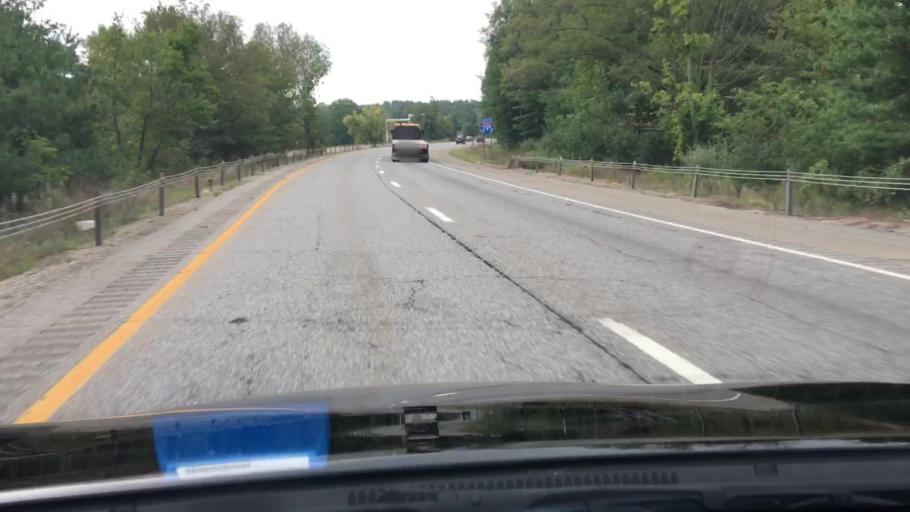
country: US
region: Connecticut
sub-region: Windham County
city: Putnam
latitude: 41.8941
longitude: -71.8968
